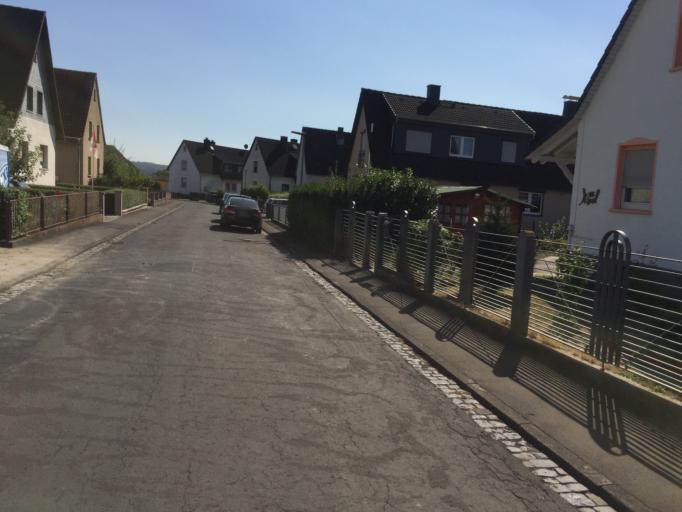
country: DE
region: Hesse
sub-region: Regierungsbezirk Giessen
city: Hungen
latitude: 50.4348
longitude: 8.8820
